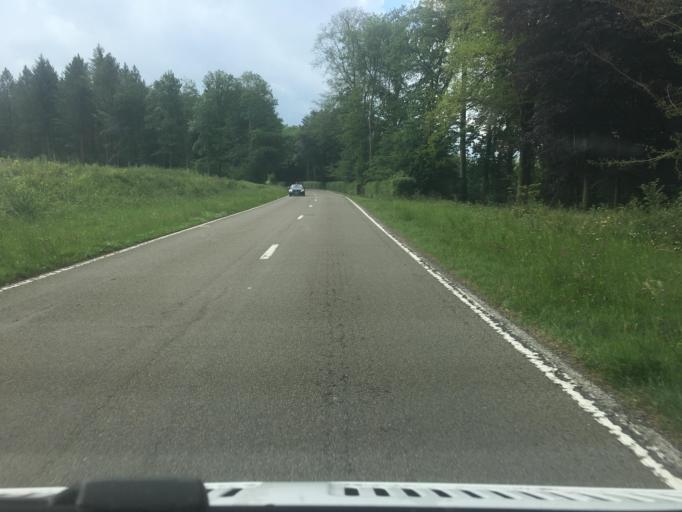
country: BE
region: Wallonia
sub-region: Province du Luxembourg
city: Florenville
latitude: 49.6498
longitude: 5.3386
